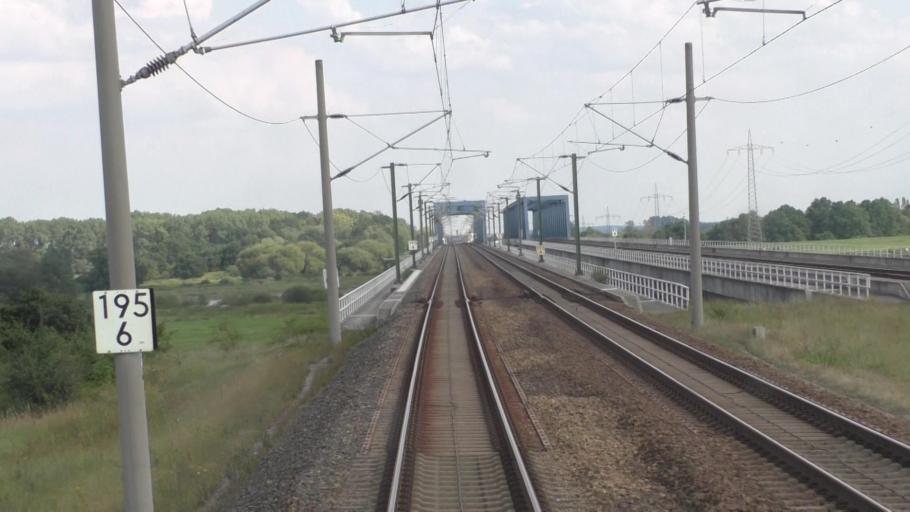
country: DE
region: Saxony-Anhalt
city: Schonhausen
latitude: 52.5991
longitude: 11.9932
